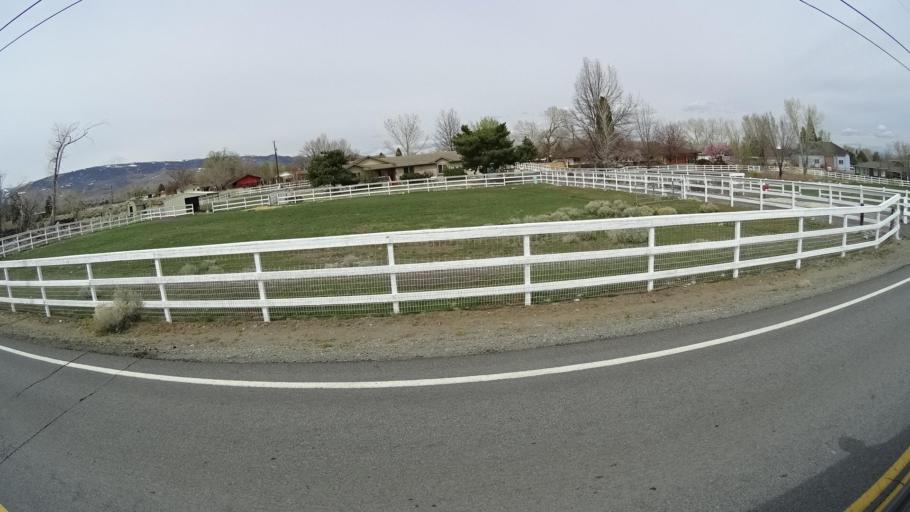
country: US
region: Nevada
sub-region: Washoe County
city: Sparks
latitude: 39.4366
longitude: -119.7723
